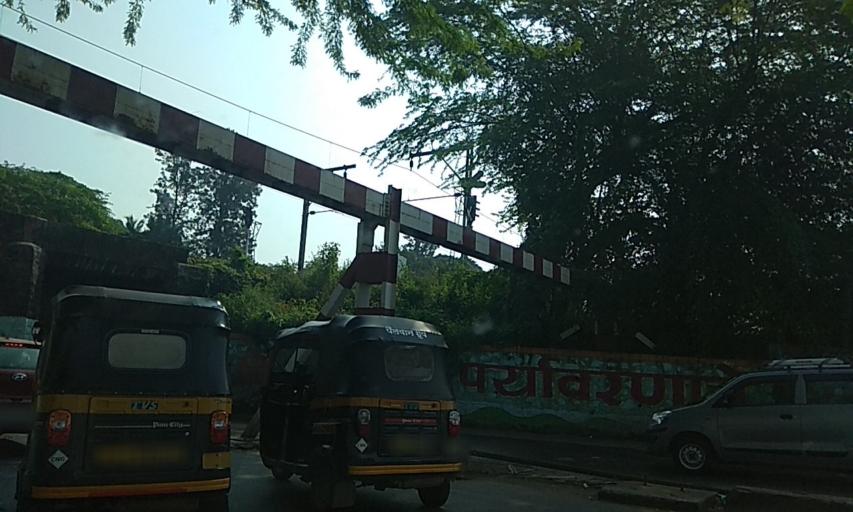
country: IN
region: Maharashtra
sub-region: Pune Division
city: Khadki
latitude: 18.5570
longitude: 73.8443
